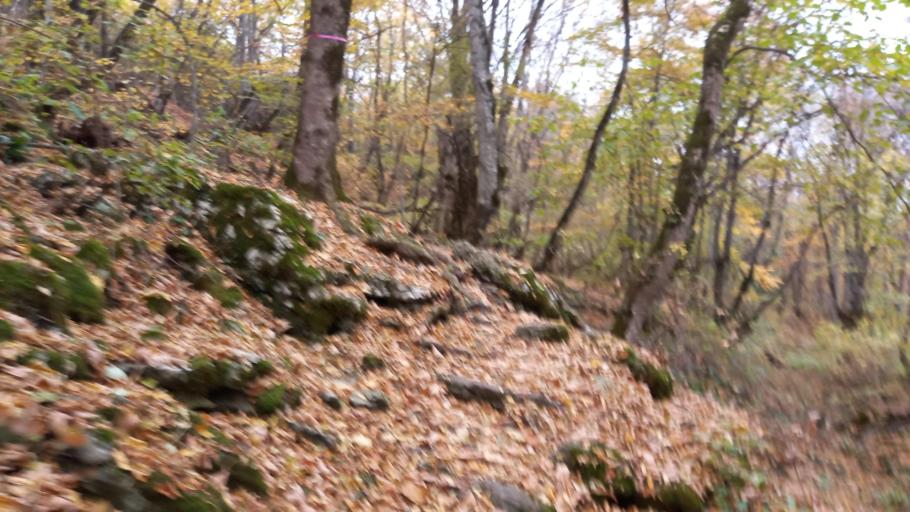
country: RU
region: Krasnodarskiy
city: Gubskaya
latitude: 44.2801
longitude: 40.5245
